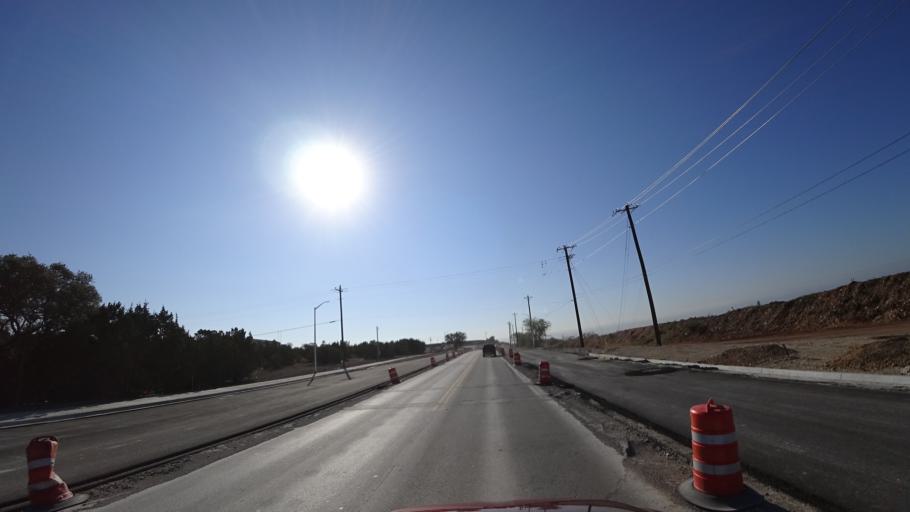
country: US
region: Texas
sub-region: Williamson County
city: Cedar Park
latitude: 30.5099
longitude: -97.8573
